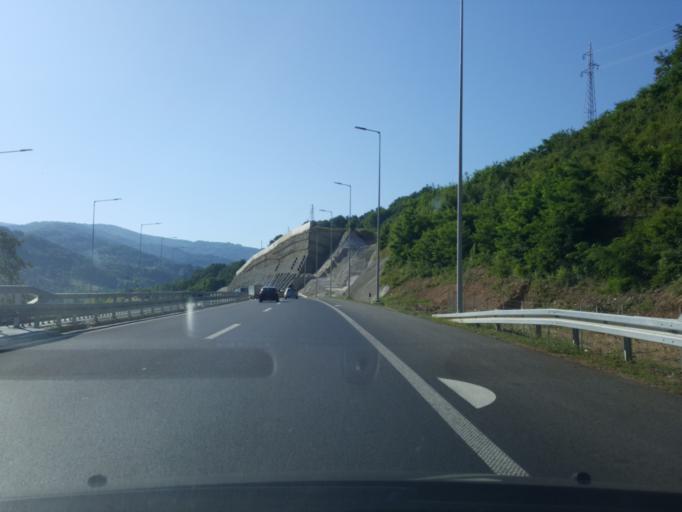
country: RS
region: Central Serbia
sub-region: Jablanicki Okrug
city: Vlasotince
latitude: 42.8669
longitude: 22.1066
